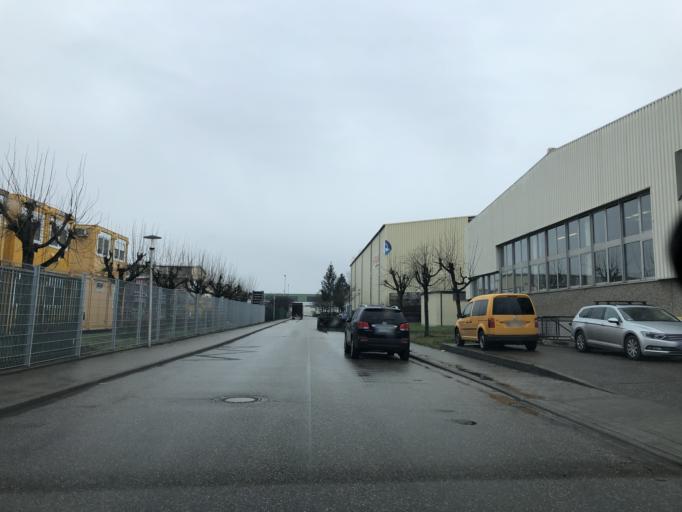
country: DE
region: Baden-Wuerttemberg
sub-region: Karlsruhe Region
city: Rastatt
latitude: 48.8586
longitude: 8.2272
